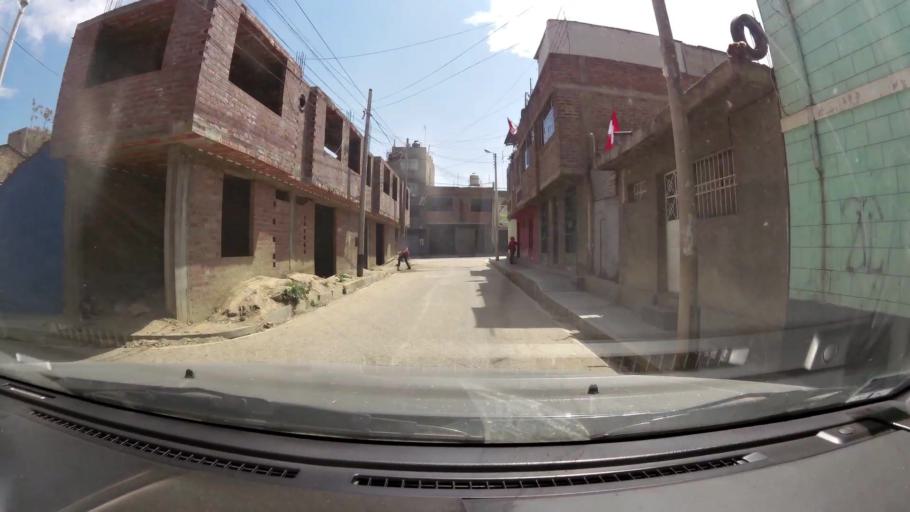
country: PE
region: Junin
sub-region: Provincia de Huancayo
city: Huancayo
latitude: -12.0837
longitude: -75.2058
